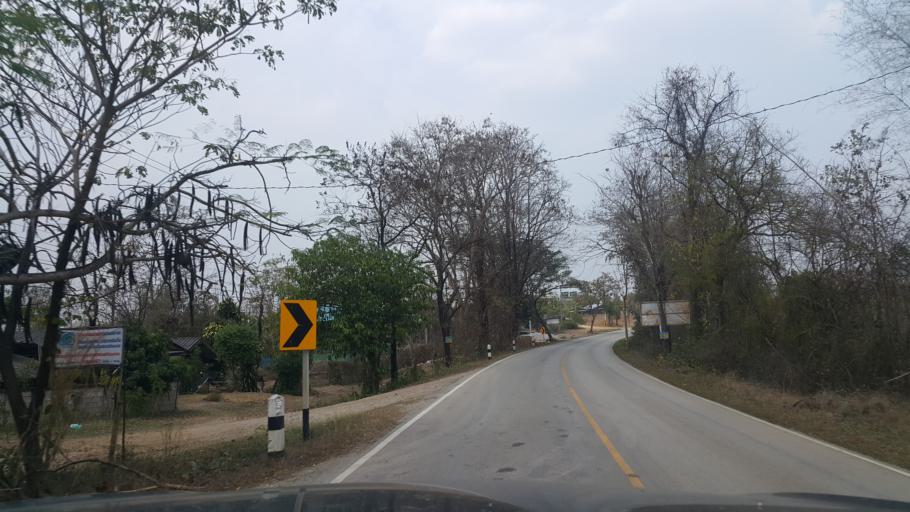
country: TH
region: Lampang
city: Soem Ngam
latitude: 17.9913
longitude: 99.1691
